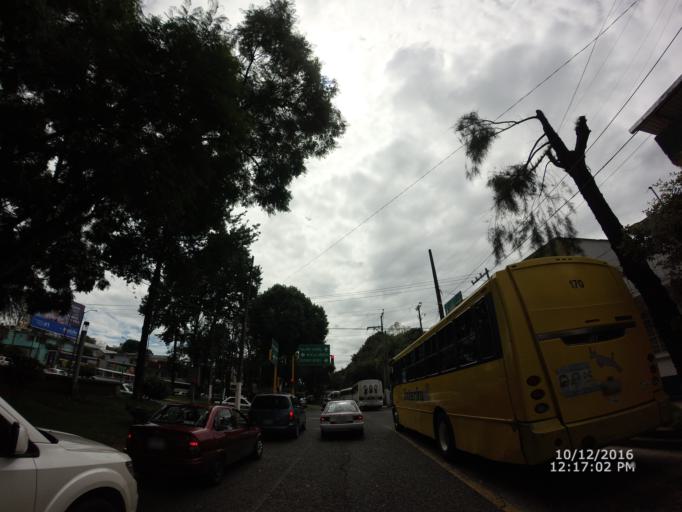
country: MX
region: Veracruz
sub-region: Xalapa
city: Xalapa de Enriquez
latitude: 19.5433
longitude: -96.9276
